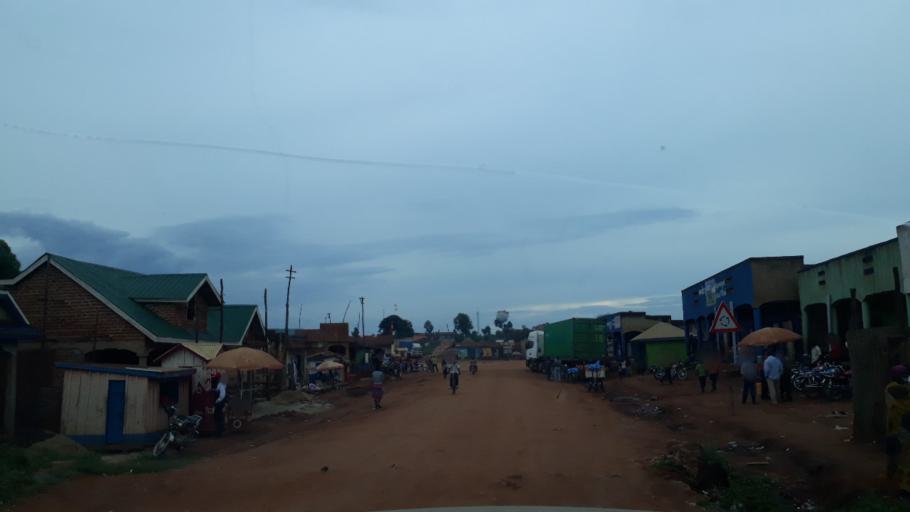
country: UG
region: Northern Region
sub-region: Zombo District
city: Paidha
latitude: 2.2229
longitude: 30.7928
